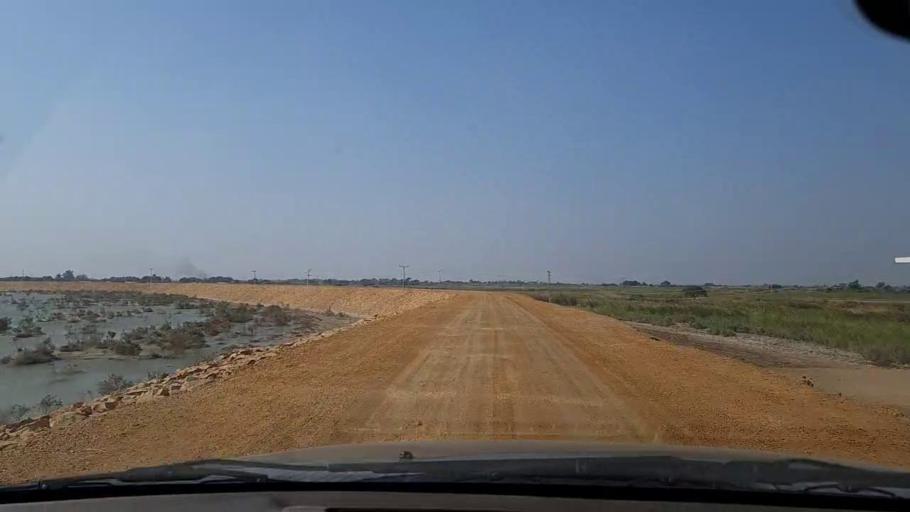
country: PK
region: Sindh
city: Chuhar Jamali
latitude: 24.4566
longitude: 67.8682
